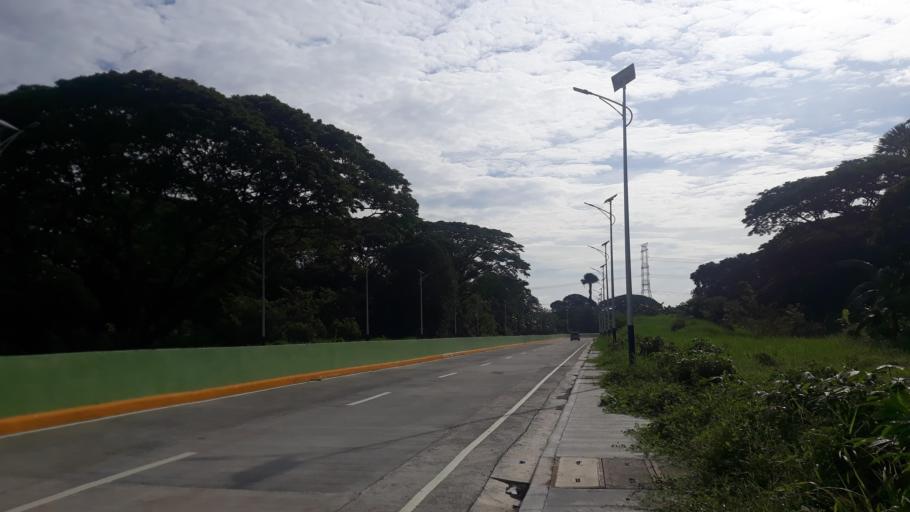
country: PH
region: Calabarzon
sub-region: Province of Cavite
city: Biga
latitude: 14.2885
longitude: 120.9642
